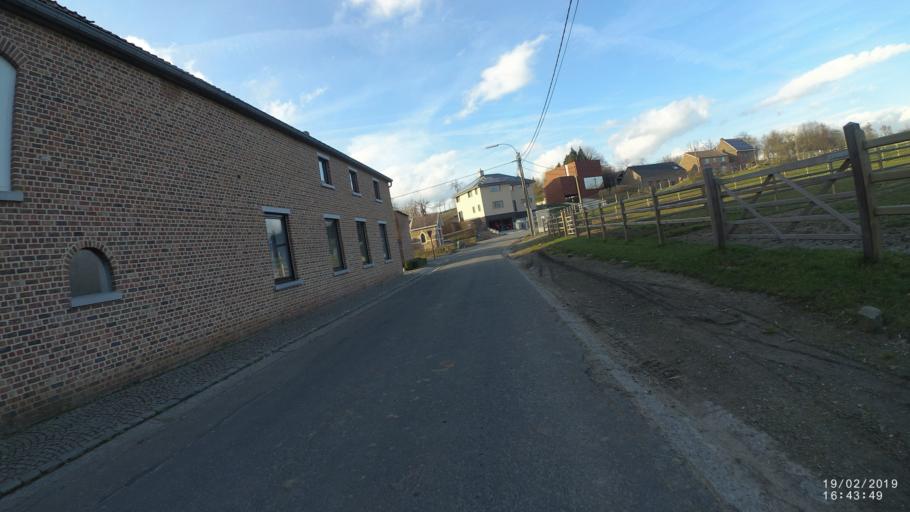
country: BE
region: Flanders
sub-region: Provincie Limburg
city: Borgloon
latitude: 50.8094
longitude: 5.3302
